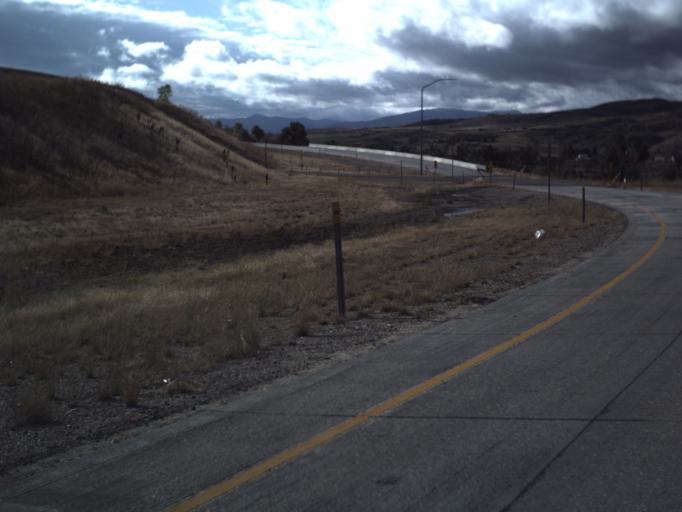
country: US
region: Utah
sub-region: Morgan County
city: Mountain Green
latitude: 41.1164
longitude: -111.7646
